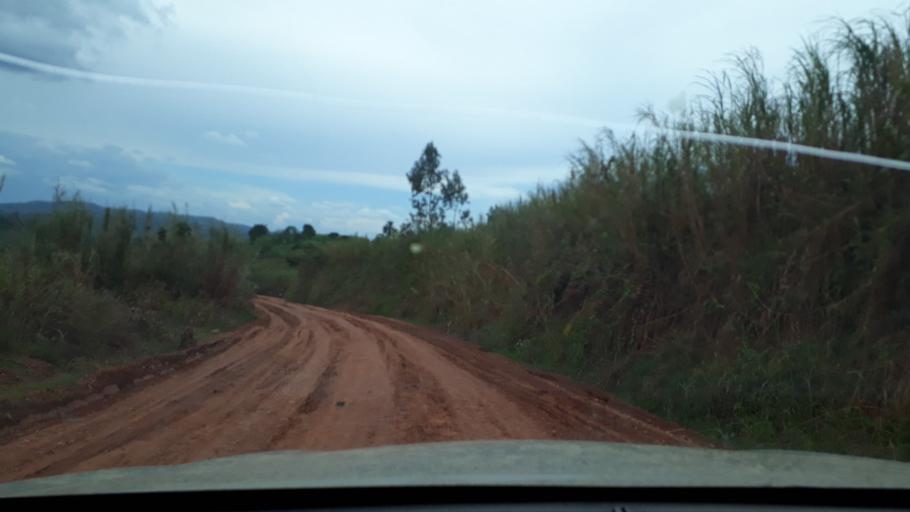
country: CD
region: Eastern Province
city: Bunia
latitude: 1.7611
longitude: 30.3823
